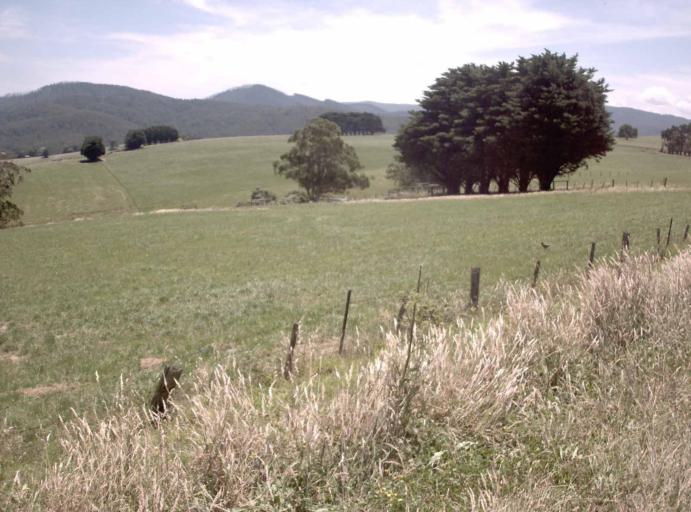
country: AU
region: Victoria
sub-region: Baw Baw
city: Warragul
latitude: -37.9923
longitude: 145.9485
